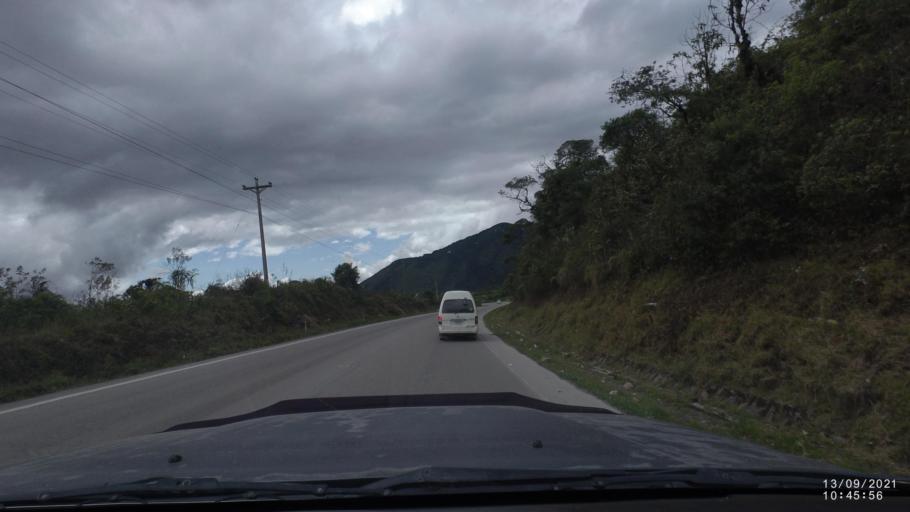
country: BO
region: Cochabamba
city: Colomi
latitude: -17.2036
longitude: -65.8709
